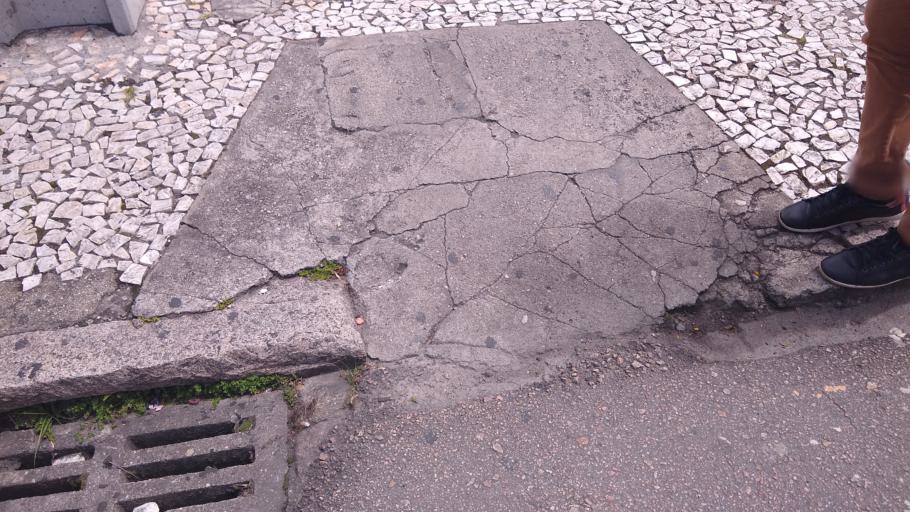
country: BR
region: Parana
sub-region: Curitiba
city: Curitiba
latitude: -25.4241
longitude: -49.2701
